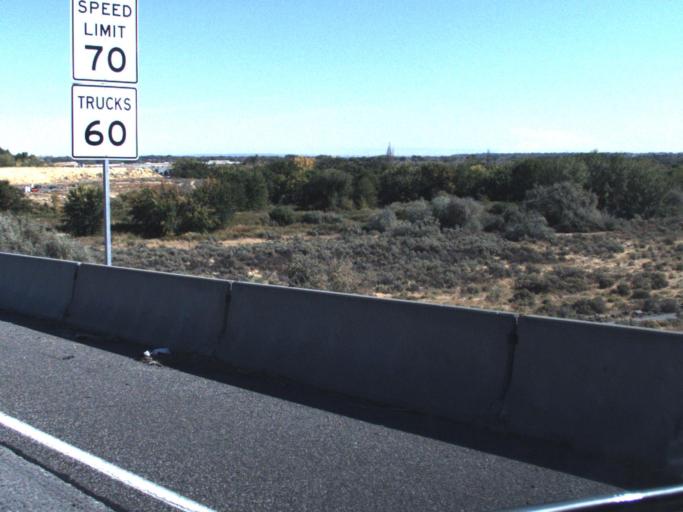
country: US
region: Washington
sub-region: Benton County
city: Richland
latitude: 46.2575
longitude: -119.2943
